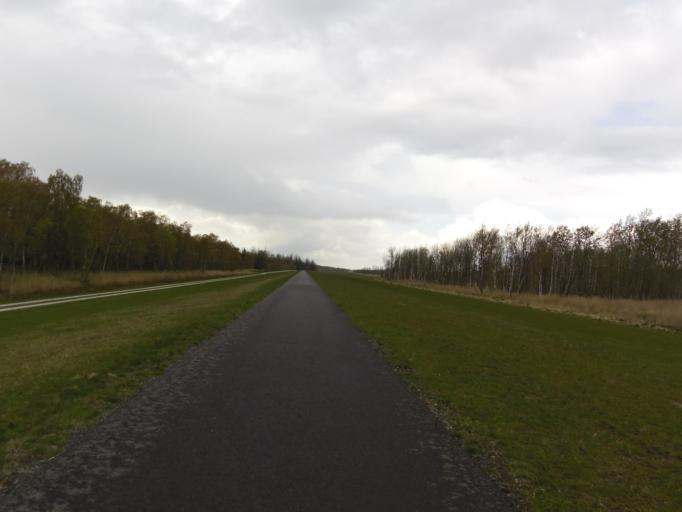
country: DE
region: Mecklenburg-Vorpommern
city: Altenpleen
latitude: 54.4310
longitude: 12.8824
